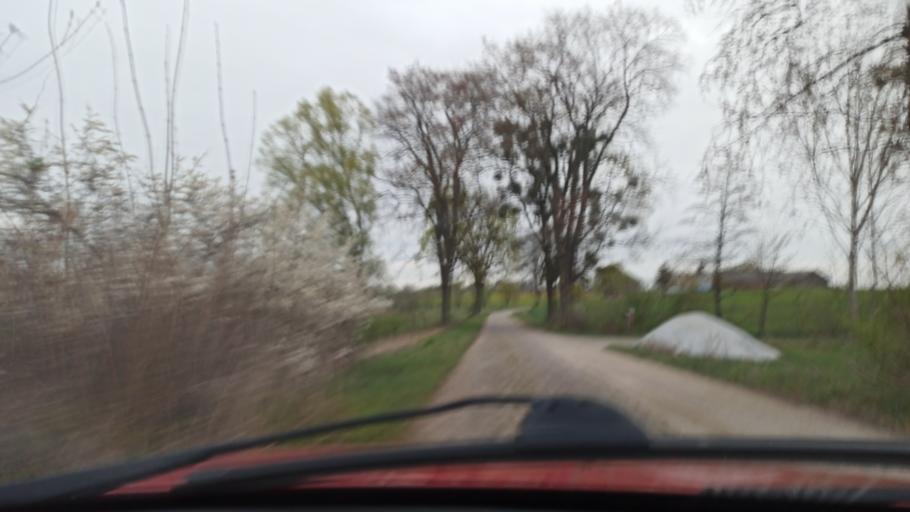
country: PL
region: Kujawsko-Pomorskie
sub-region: Powiat grudziadzki
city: Lasin
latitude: 53.5695
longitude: 19.0799
